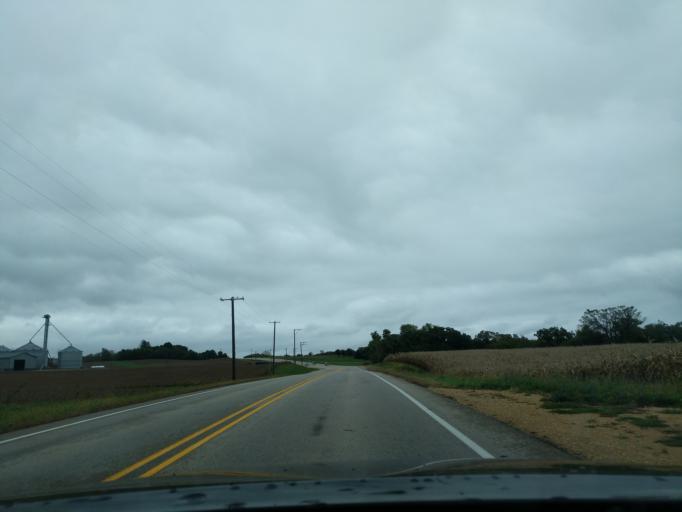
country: US
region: Illinois
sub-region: Ogle County
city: Mount Morris
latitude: 41.9956
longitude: -89.3989
